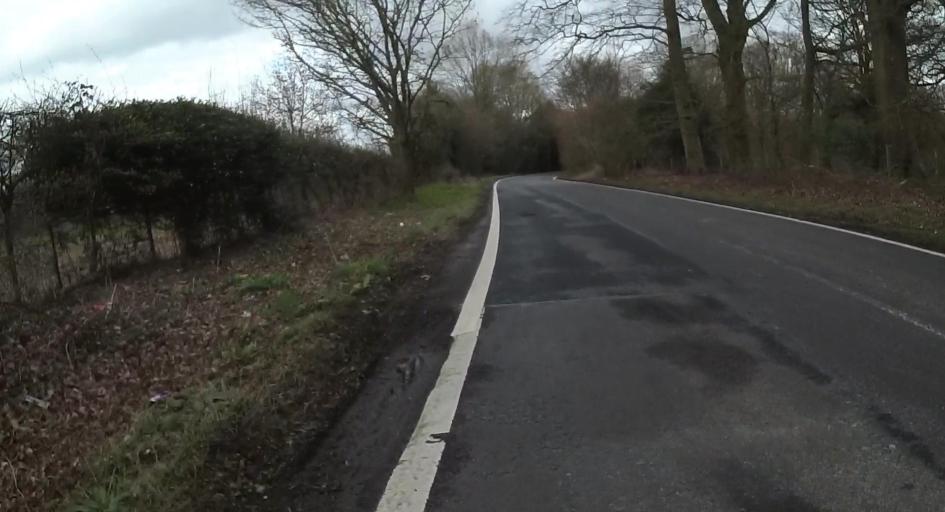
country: GB
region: England
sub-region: Hampshire
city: Alton
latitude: 51.1907
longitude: -1.0368
